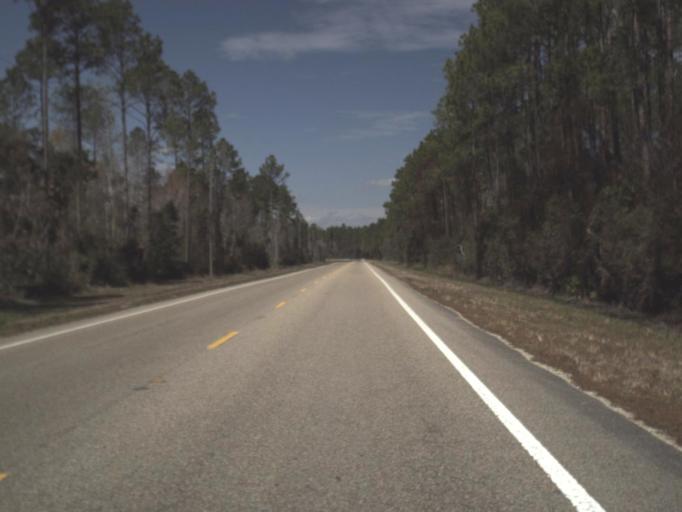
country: US
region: Florida
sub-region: Leon County
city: Woodville
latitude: 30.2166
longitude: -84.1991
